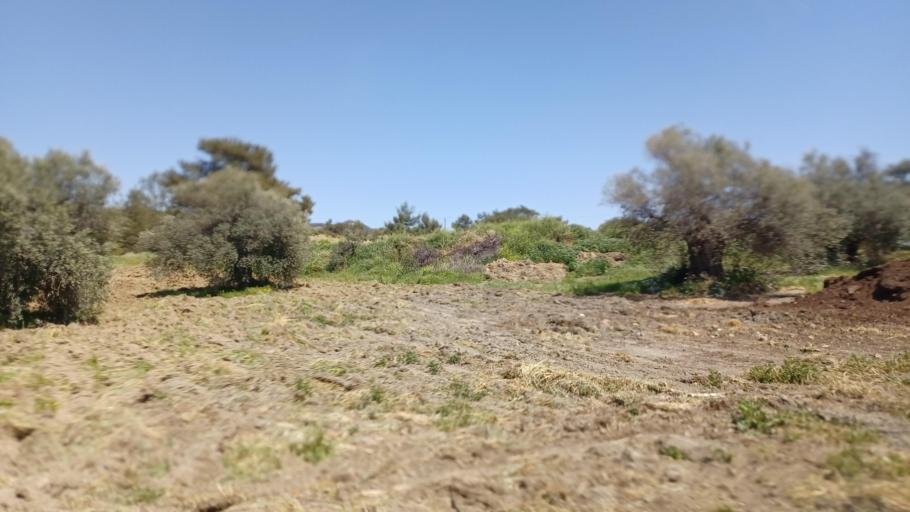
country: CY
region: Limassol
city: Parekklisha
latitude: 34.7998
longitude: 33.1349
